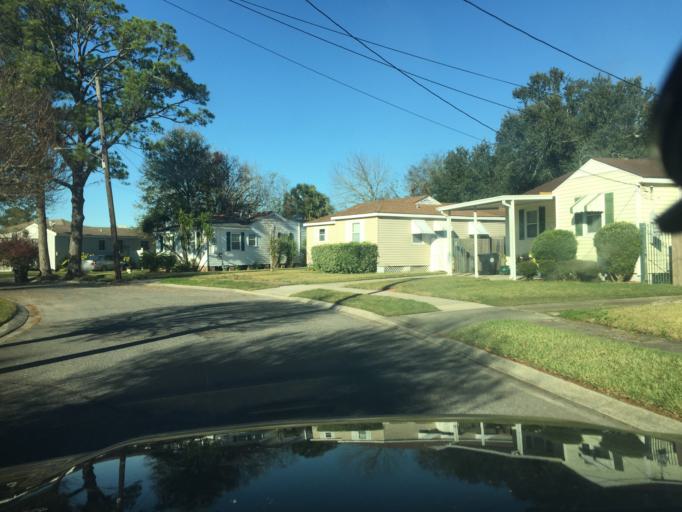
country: US
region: Louisiana
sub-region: Orleans Parish
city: New Orleans
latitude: 29.9894
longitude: -90.0778
